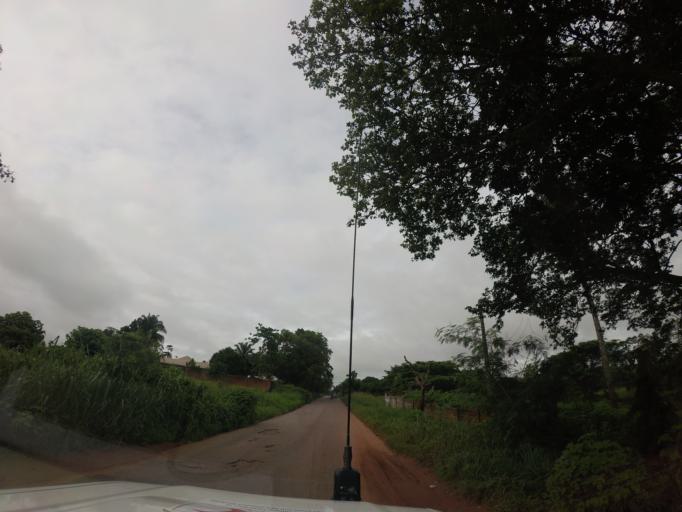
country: GN
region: Kindia
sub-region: Kindia
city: Kindia
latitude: 9.9886
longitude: -12.9114
